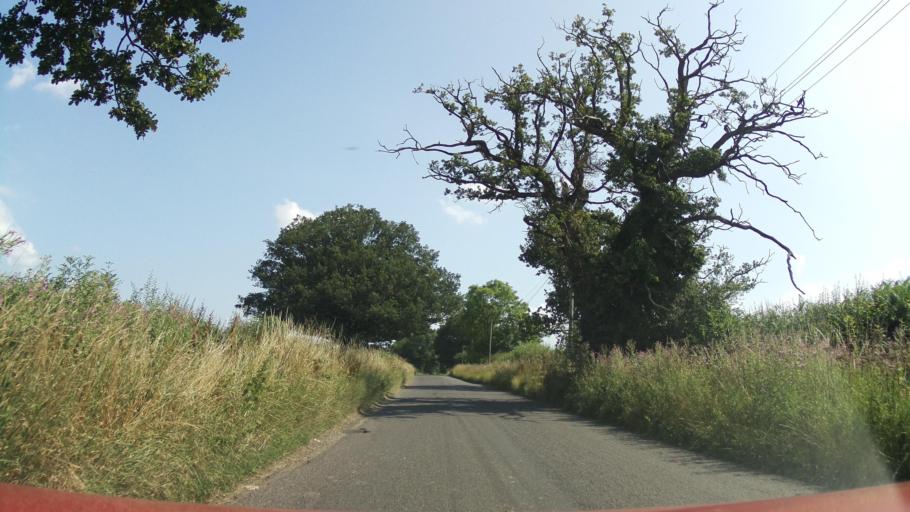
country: GB
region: England
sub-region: Wiltshire
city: Chippenham
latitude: 51.5198
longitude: -2.1083
